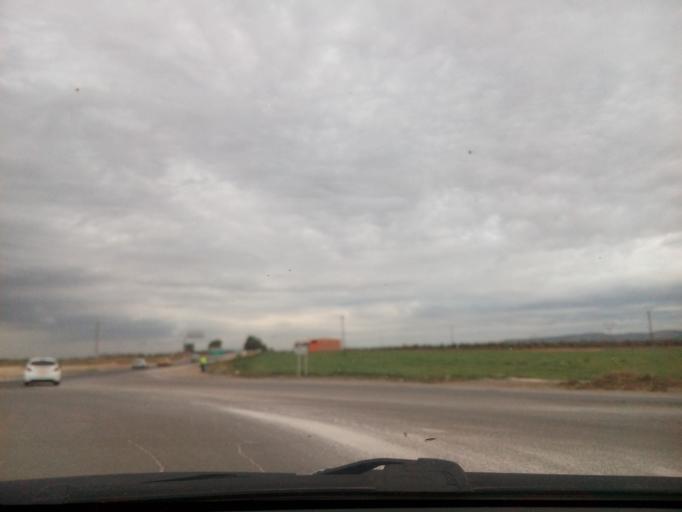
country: DZ
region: Mascara
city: Sig
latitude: 35.5363
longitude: -0.3780
